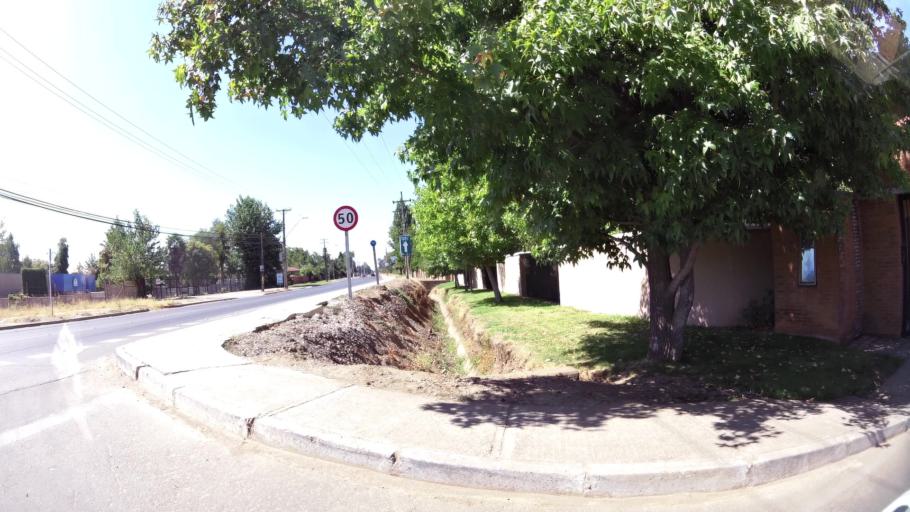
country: CL
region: Maule
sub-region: Provincia de Talca
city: Talca
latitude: -35.4356
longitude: -71.6100
